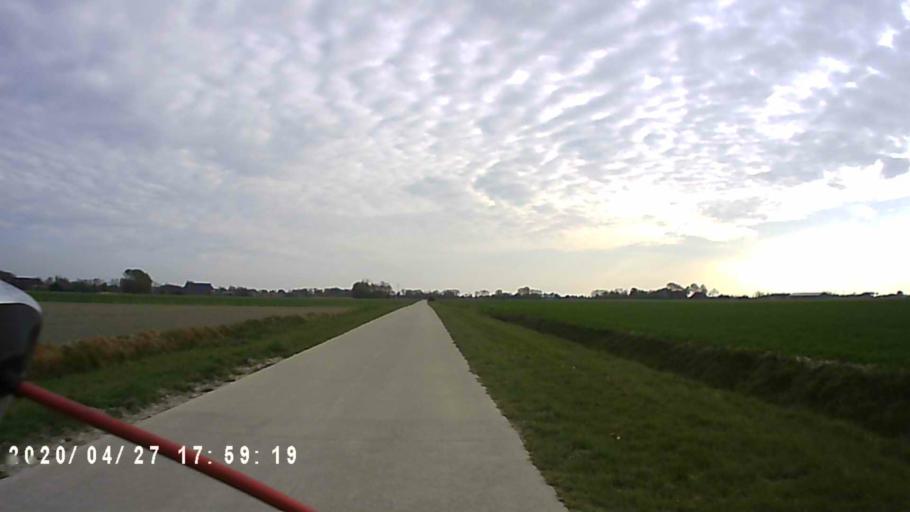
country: NL
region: Groningen
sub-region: Gemeente Winsum
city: Winsum
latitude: 53.4116
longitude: 6.4554
